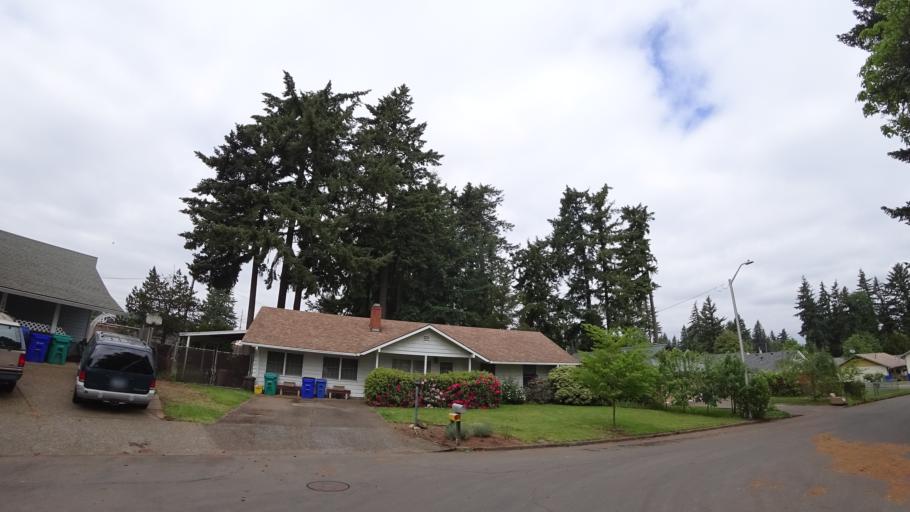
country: US
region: Oregon
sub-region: Multnomah County
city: Gresham
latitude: 45.4975
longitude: -122.4826
